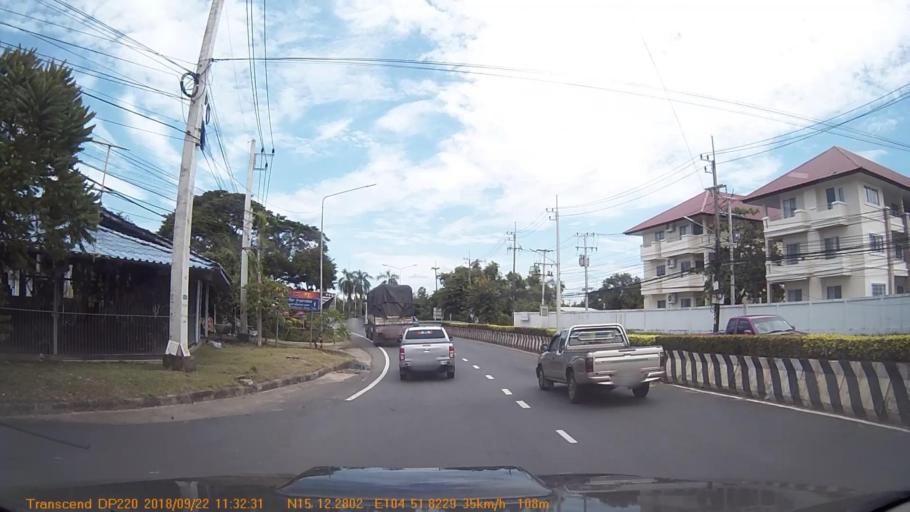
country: TH
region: Changwat Ubon Ratchathani
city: Warin Chamrap
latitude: 15.2046
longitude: 104.8637
